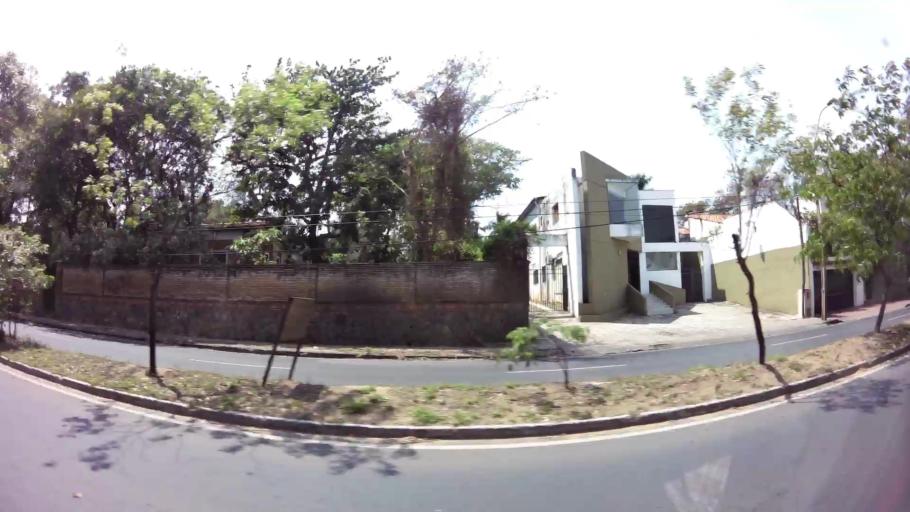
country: PY
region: Asuncion
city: Asuncion
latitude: -25.2806
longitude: -57.5869
